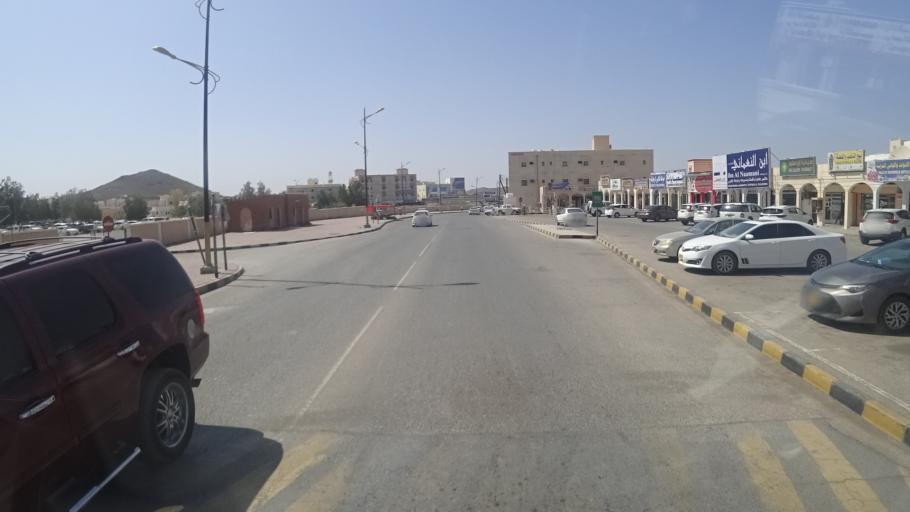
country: OM
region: Ash Sharqiyah
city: Ibra'
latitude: 22.6930
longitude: 58.5449
